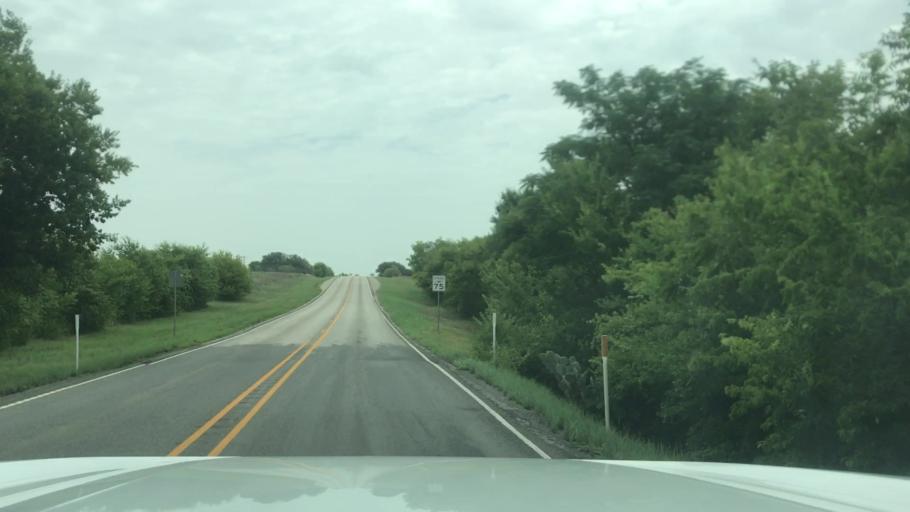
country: US
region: Texas
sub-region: Erath County
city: Dublin
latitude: 32.0577
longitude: -98.1962
